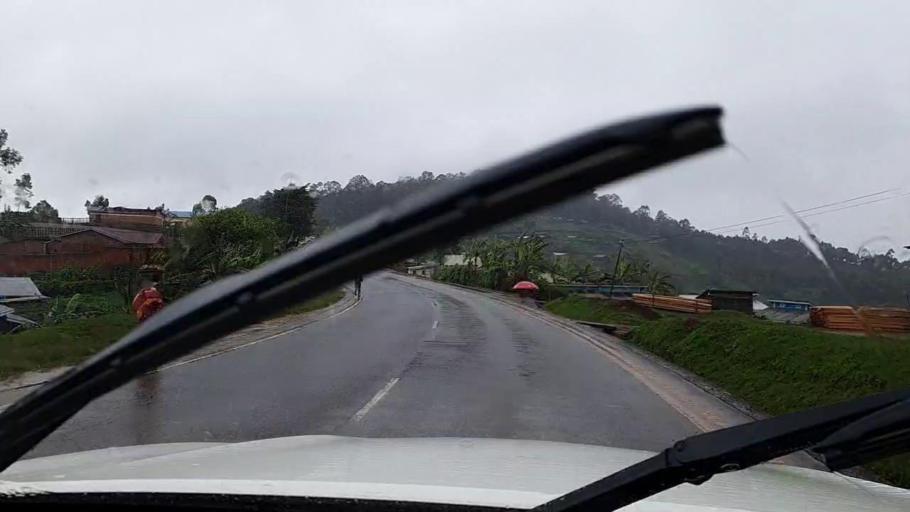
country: RW
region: Western Province
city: Cyangugu
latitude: -2.4627
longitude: 28.9984
